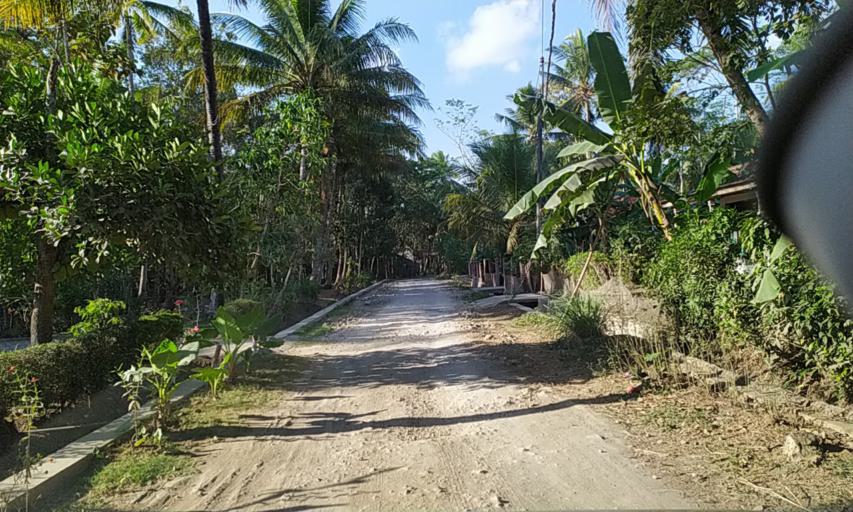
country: ID
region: Central Java
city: Tambaksari
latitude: -7.4958
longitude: 108.7596
